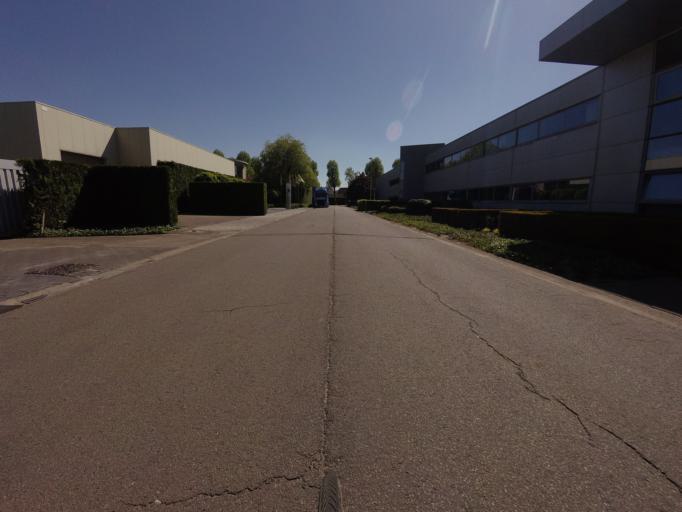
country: BE
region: Flanders
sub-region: Provincie Antwerpen
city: Boechout
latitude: 51.1679
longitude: 4.4889
